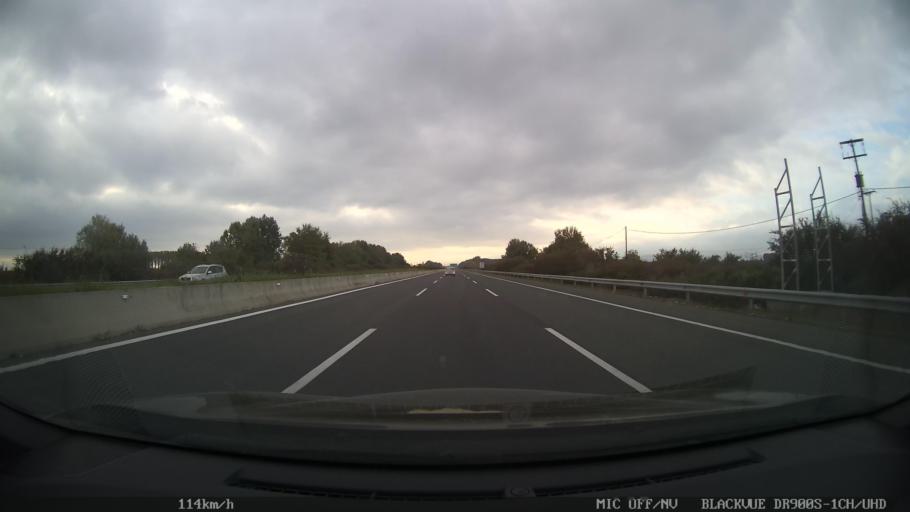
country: GR
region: Central Macedonia
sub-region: Nomos Pierias
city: Nea Efesos
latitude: 40.2140
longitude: 22.5433
